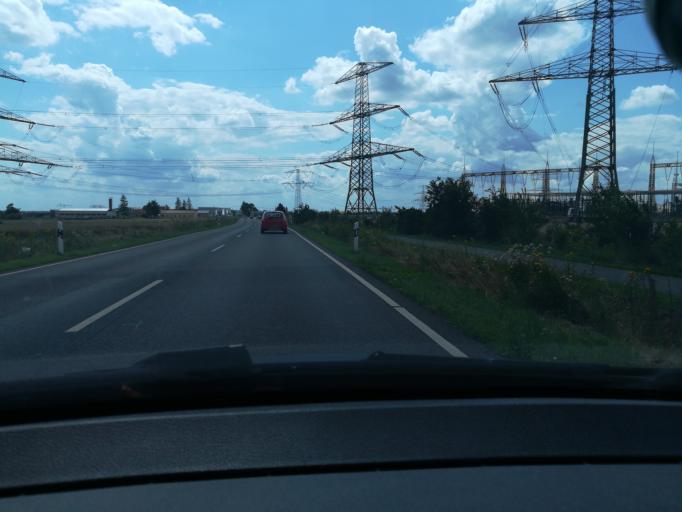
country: DE
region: Saxony-Anhalt
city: Wolmirstedt
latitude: 52.2685
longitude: 11.6446
